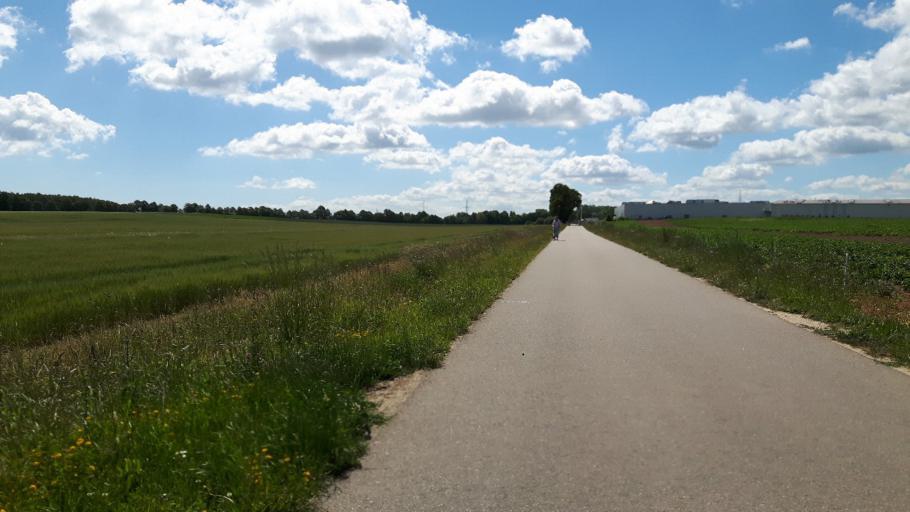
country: PL
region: Pomeranian Voivodeship
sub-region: Gdynia
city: Pogorze
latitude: 54.5695
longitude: 18.5020
